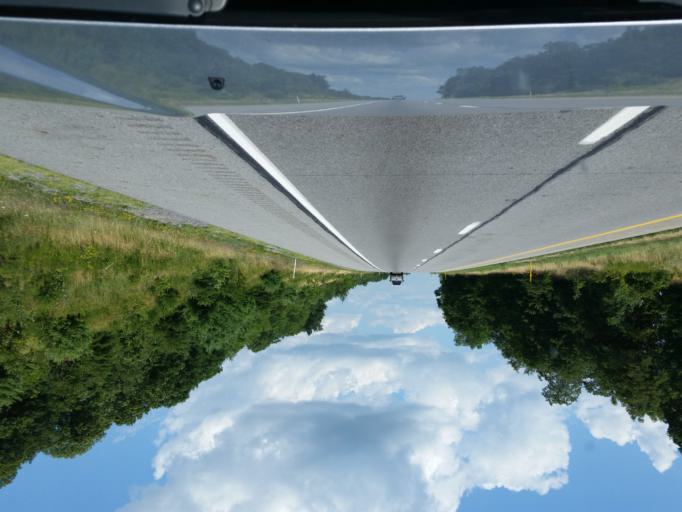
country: US
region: Pennsylvania
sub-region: Blair County
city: Claysburg
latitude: 40.1673
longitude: -78.4955
